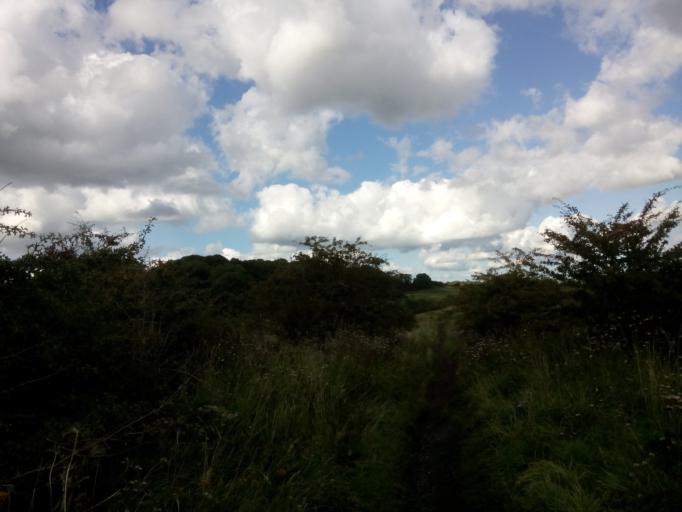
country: GB
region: England
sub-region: County Durham
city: Pittington
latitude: 54.7837
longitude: -1.5127
